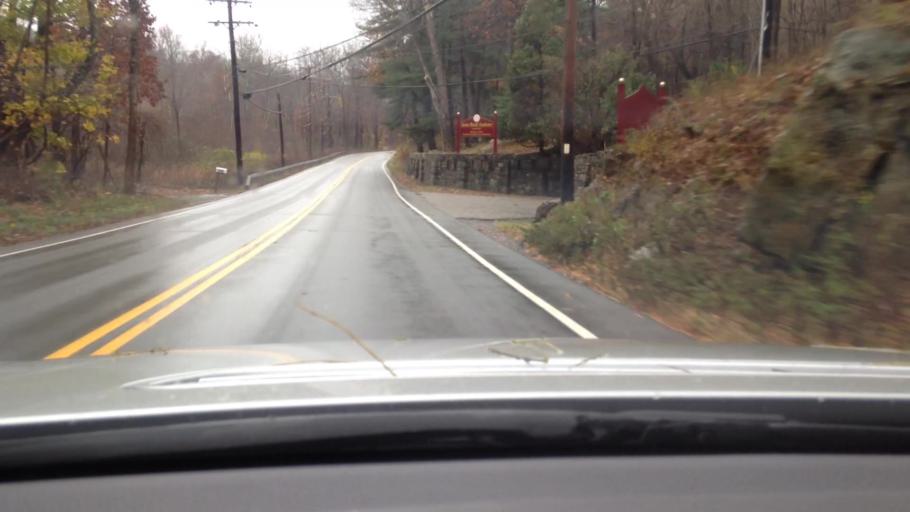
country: US
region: New York
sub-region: Orange County
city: West Point
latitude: 41.3981
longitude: -73.9333
